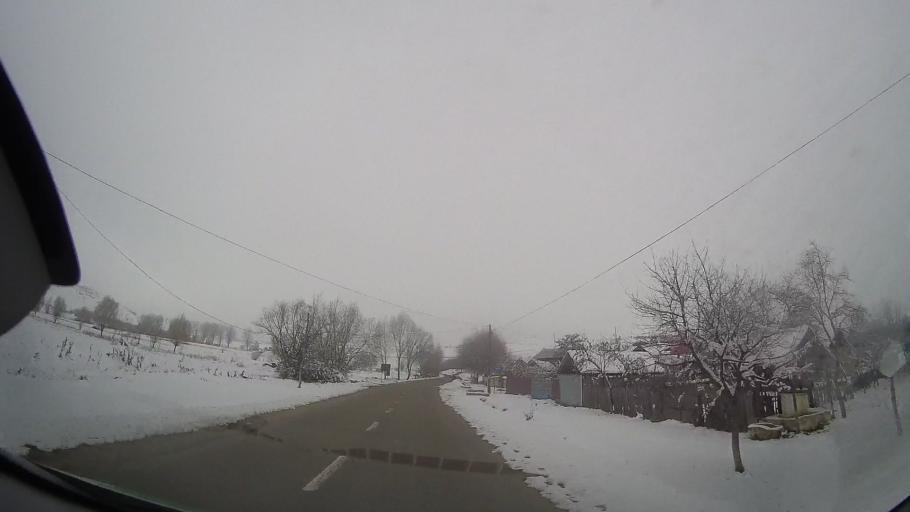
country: RO
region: Neamt
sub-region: Comuna Oniceni
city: Oniceni
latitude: 46.8008
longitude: 27.1384
